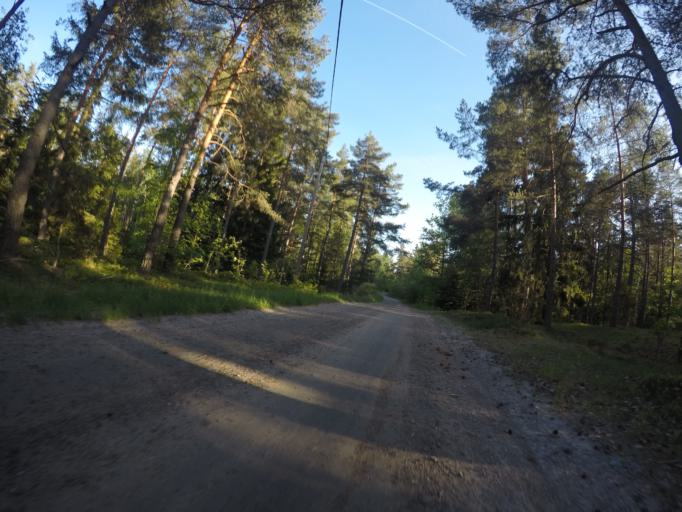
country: SE
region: Soedermanland
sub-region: Eskilstuna Kommun
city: Eskilstuna
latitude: 59.3498
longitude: 16.5343
